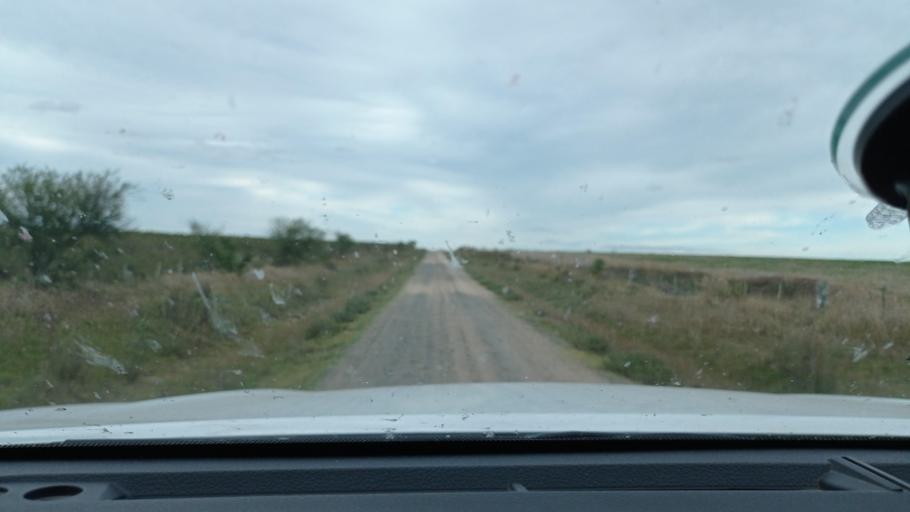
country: UY
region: Florida
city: Casupa
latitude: -34.1387
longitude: -55.7848
